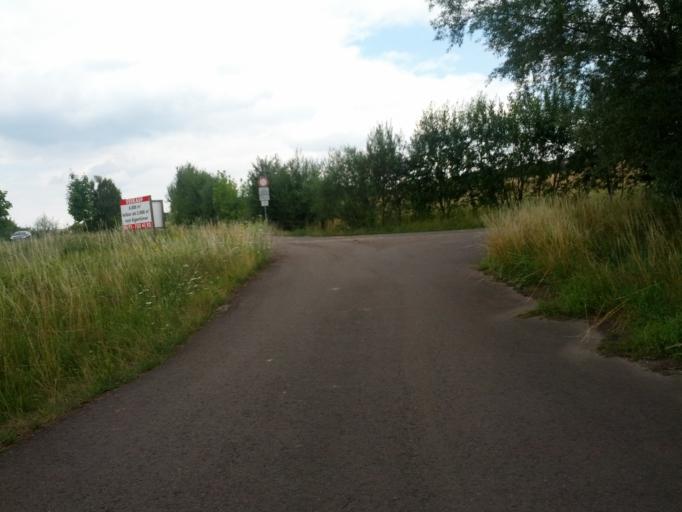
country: DE
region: Thuringia
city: Eisenach
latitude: 51.0026
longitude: 10.3203
